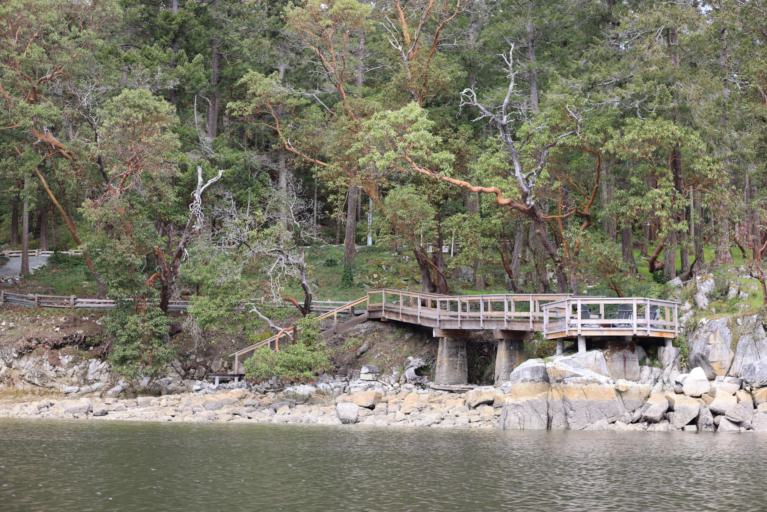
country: CA
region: British Columbia
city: North Saanich
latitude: 48.6000
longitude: -123.4776
